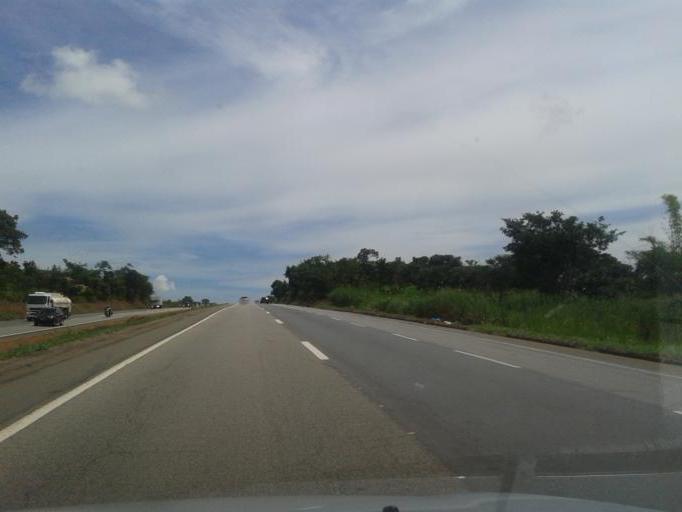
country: BR
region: Goias
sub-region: Hidrolandia
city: Hidrolandia
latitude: -17.0696
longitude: -49.2242
